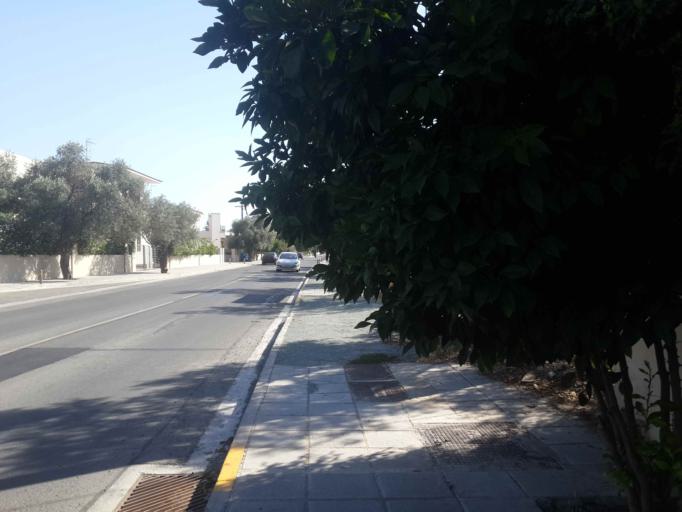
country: CY
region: Lefkosia
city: Nicosia
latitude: 35.1534
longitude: 33.3377
